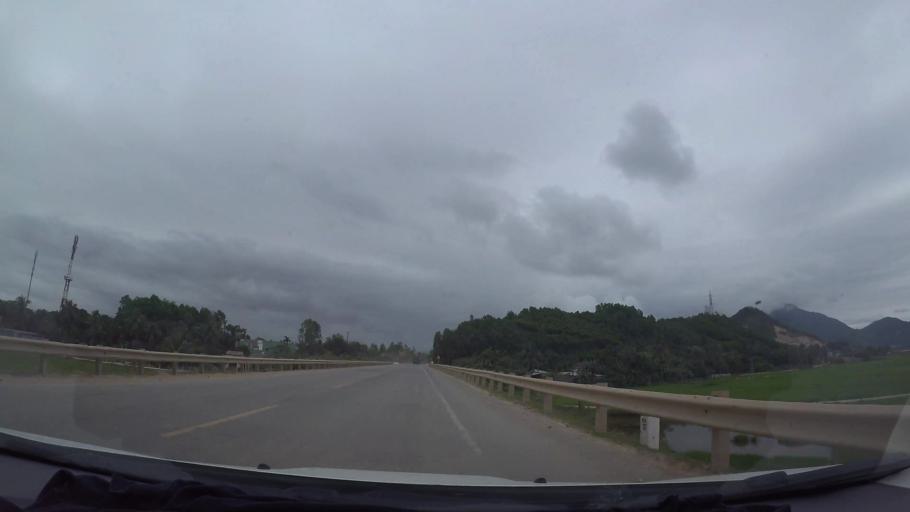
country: VN
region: Da Nang
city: Lien Chieu
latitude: 16.1033
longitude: 108.0988
